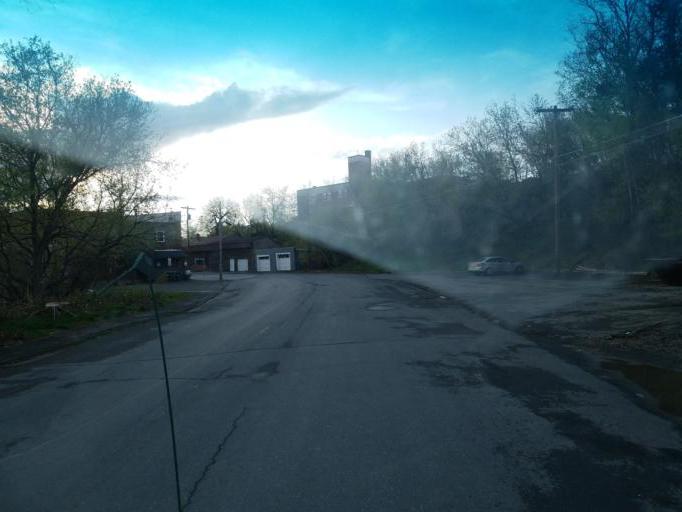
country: US
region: Maine
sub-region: Aroostook County
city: Caribou
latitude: 46.8595
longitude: -68.0099
